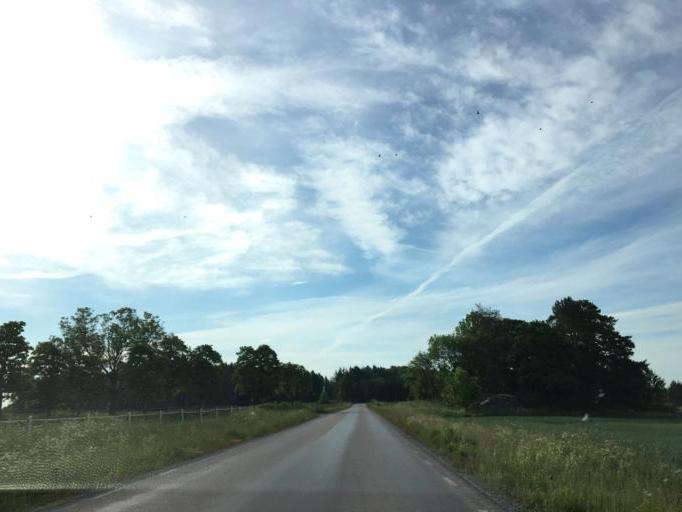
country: SE
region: Soedermanland
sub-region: Eskilstuna Kommun
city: Torshalla
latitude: 59.4167
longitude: 16.4389
